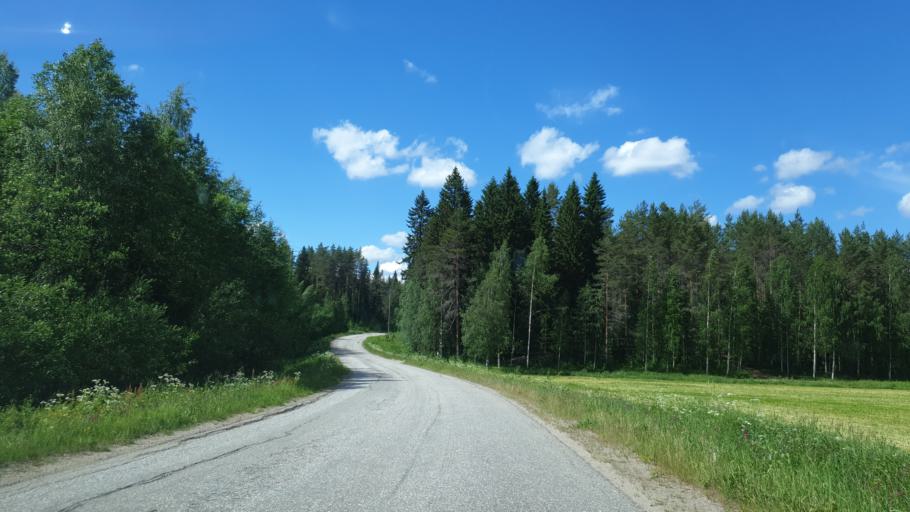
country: FI
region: Northern Savo
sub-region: Koillis-Savo
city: Kaavi
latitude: 63.0125
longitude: 28.6599
